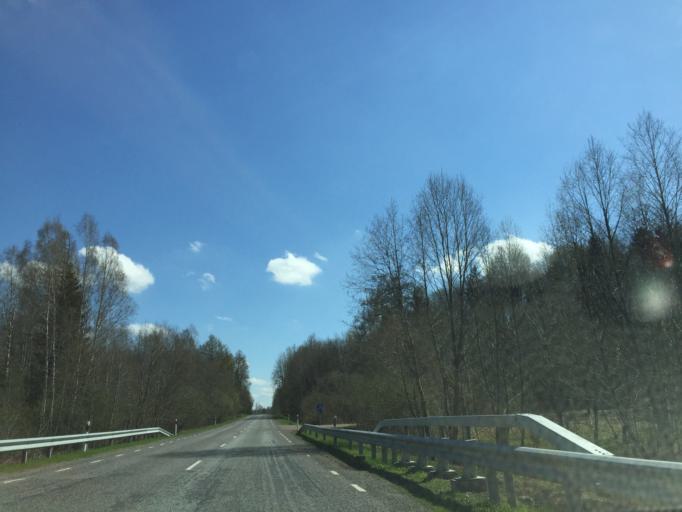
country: EE
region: Tartu
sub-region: Elva linn
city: Elva
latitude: 58.1525
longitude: 26.2236
